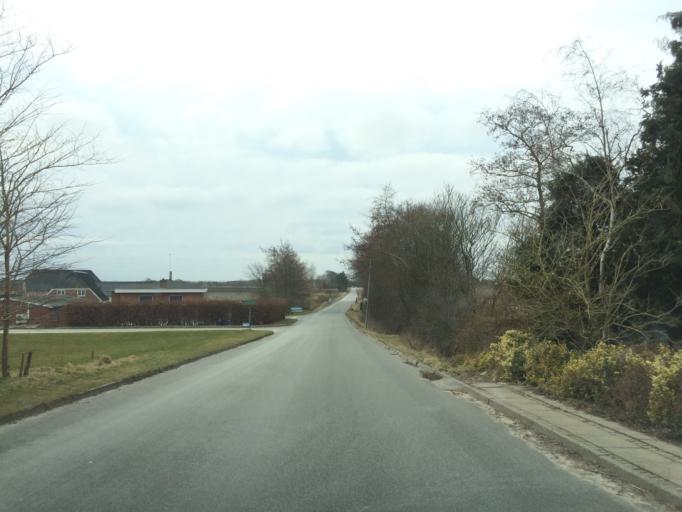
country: DK
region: South Denmark
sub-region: Varde Kommune
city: Oksbol
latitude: 55.7949
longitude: 8.3601
